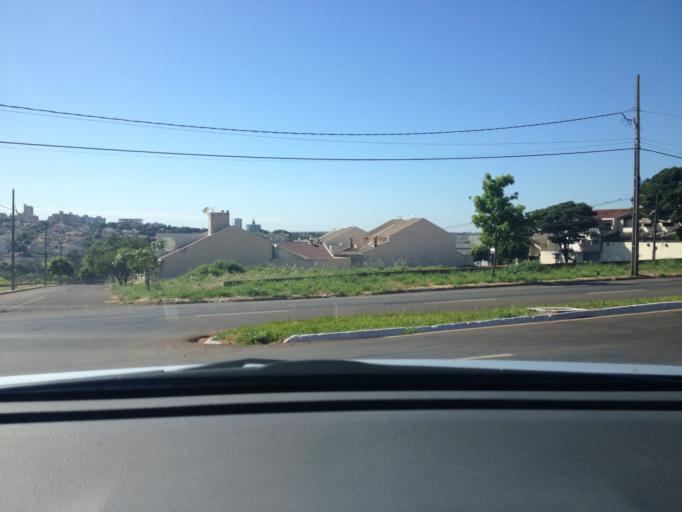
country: BR
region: Parana
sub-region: Maringa
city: Maringa
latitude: -23.4469
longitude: -51.9445
